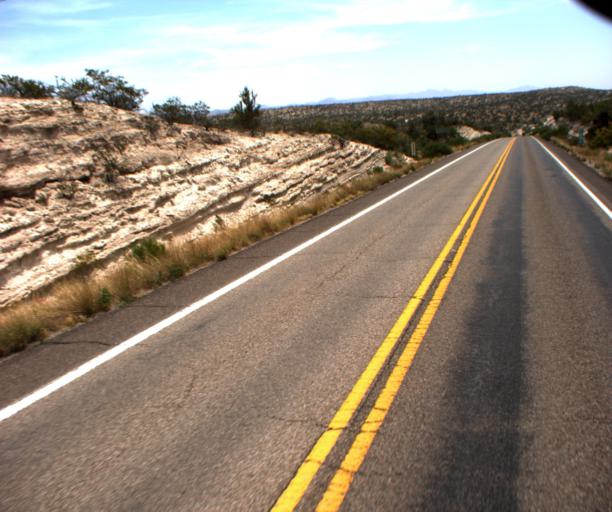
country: US
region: Arizona
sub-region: Gila County
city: Peridot
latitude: 33.2685
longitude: -110.3139
